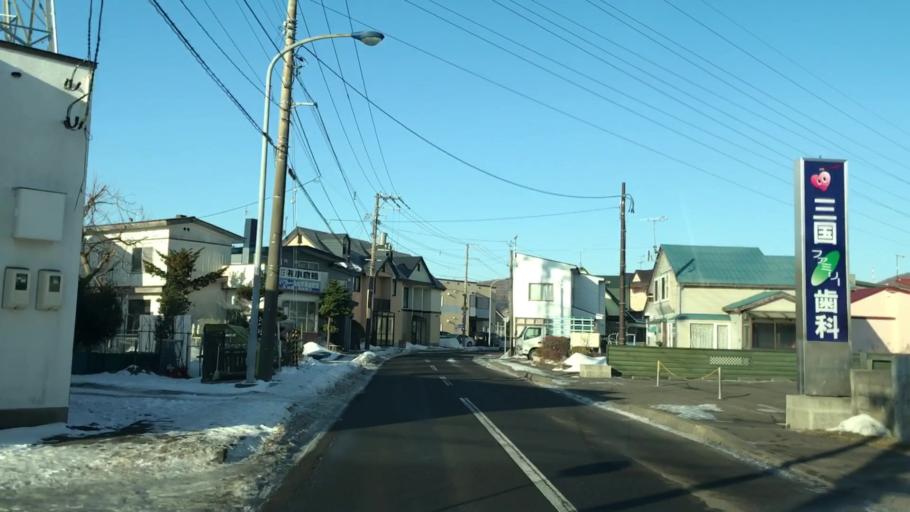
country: JP
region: Hokkaido
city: Muroran
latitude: 42.3636
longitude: 141.0457
